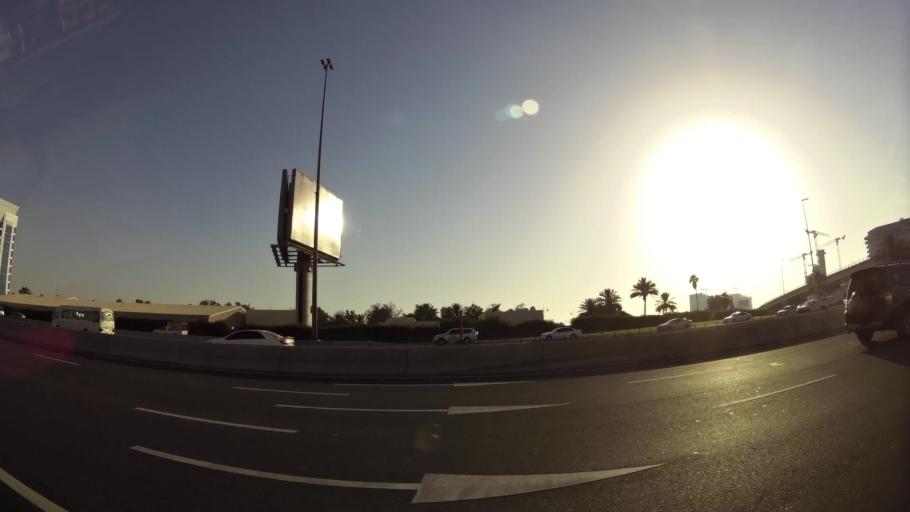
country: AE
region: Ash Shariqah
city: Sharjah
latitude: 25.2484
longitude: 55.3369
